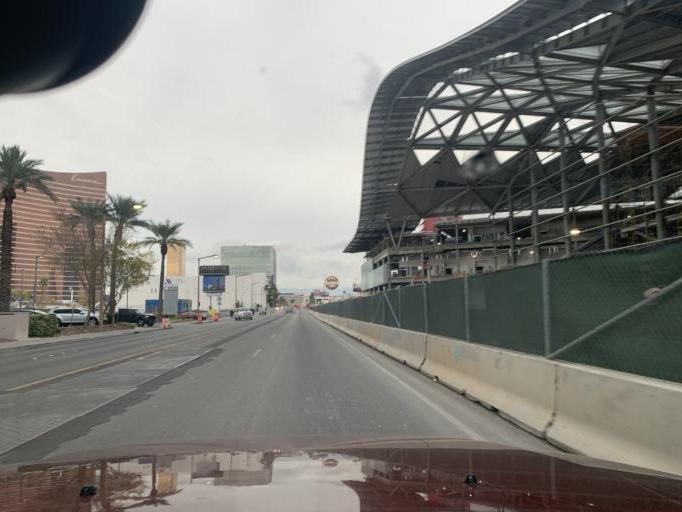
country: US
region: Nevada
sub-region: Clark County
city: Paradise
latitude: 36.1324
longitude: -115.1570
